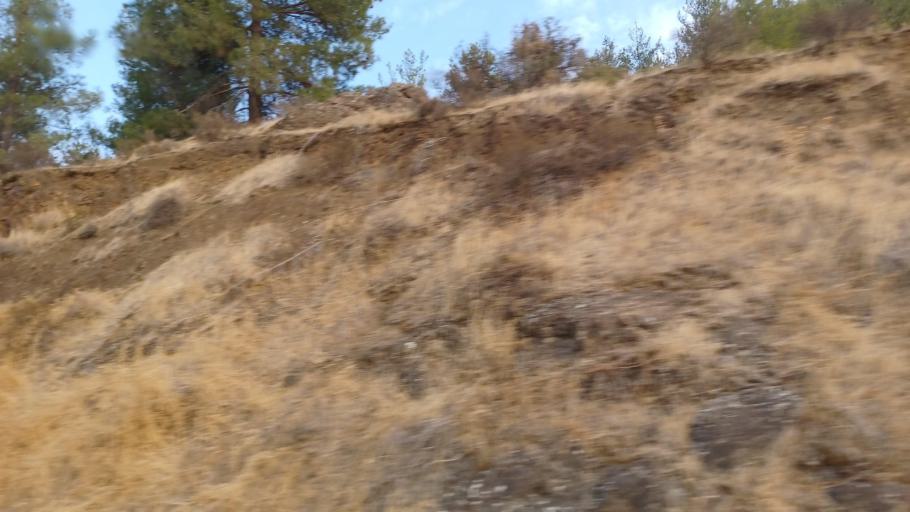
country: CY
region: Lefkosia
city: Kakopetria
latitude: 35.0235
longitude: 32.8995
